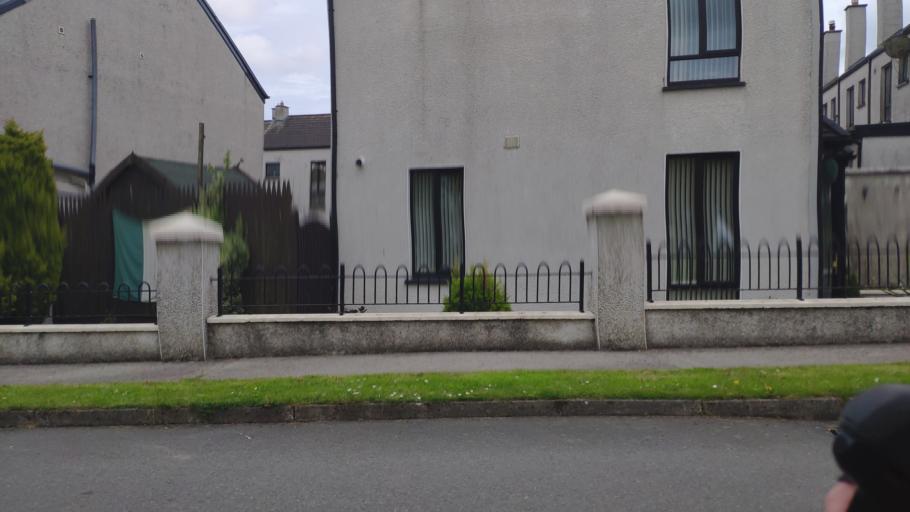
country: IE
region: Munster
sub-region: County Cork
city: Cork
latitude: 51.9123
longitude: -8.5036
